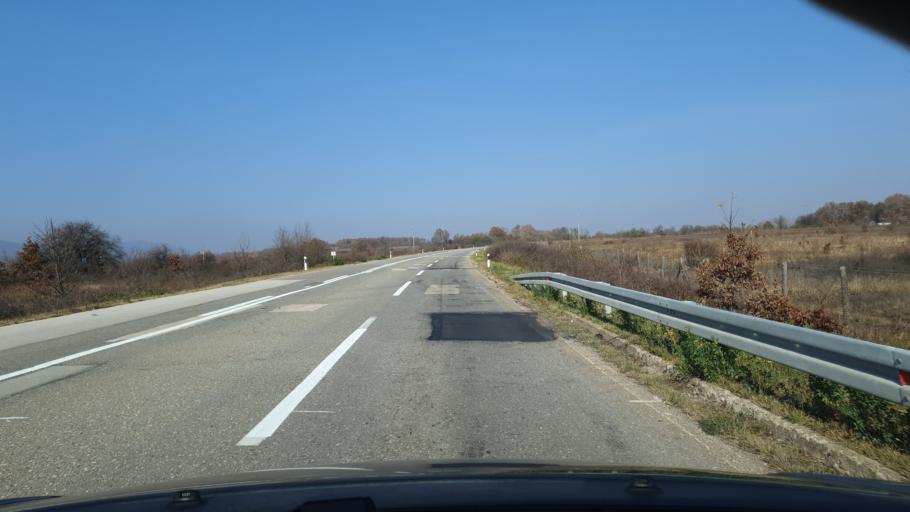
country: RS
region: Central Serbia
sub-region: Borski Okrug
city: Negotin
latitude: 44.1162
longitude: 22.3412
